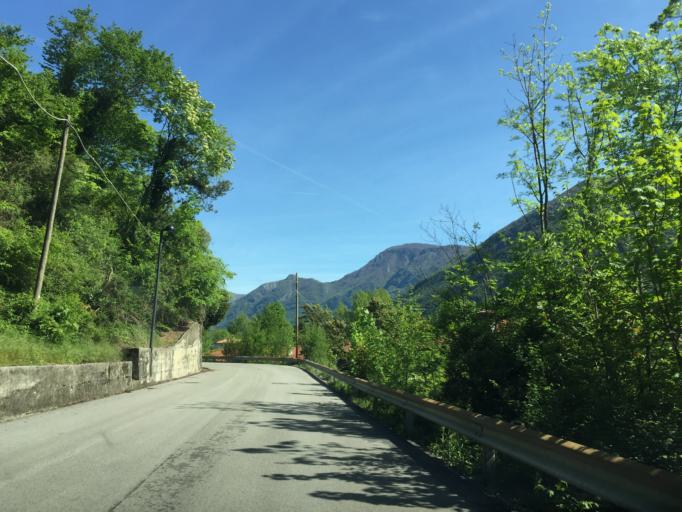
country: IT
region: Friuli Venezia Giulia
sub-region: Provincia di Udine
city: Trasaghis
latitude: 46.2958
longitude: 13.0507
